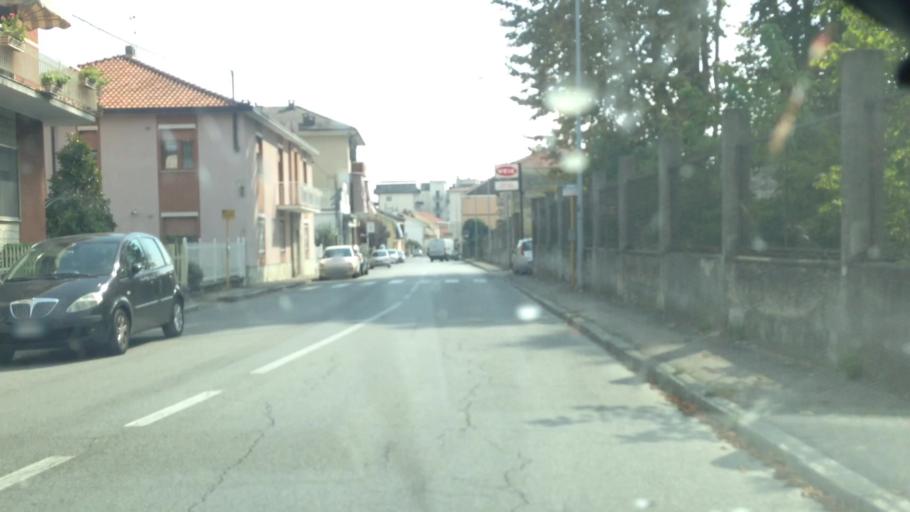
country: IT
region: Piedmont
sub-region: Provincia di Asti
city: Asti
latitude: 44.9089
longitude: 8.2120
